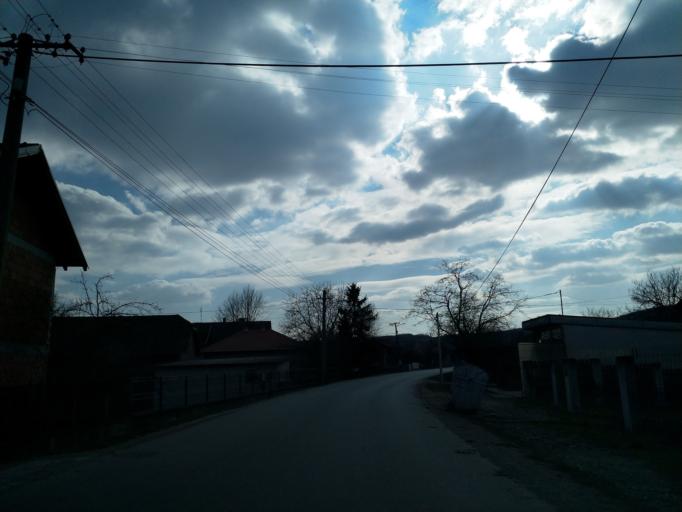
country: RS
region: Central Serbia
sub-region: Sumadijski Okrug
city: Batocina
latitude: 44.1458
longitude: 21.0766
